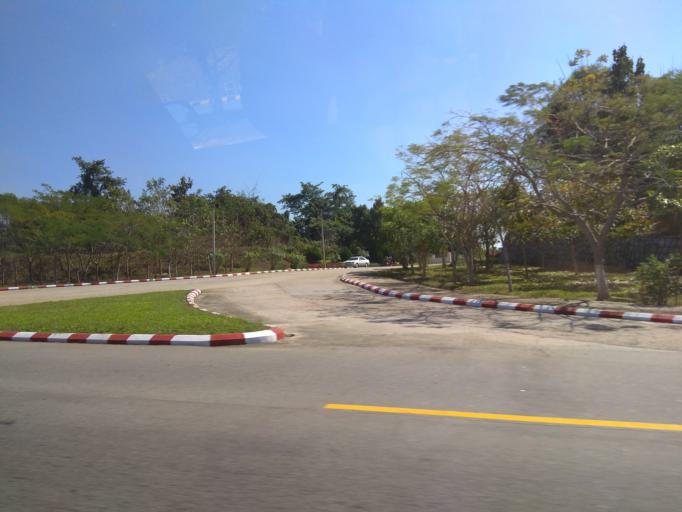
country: MM
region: Mandalay
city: Nay Pyi Taw
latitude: 19.7553
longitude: 96.1295
